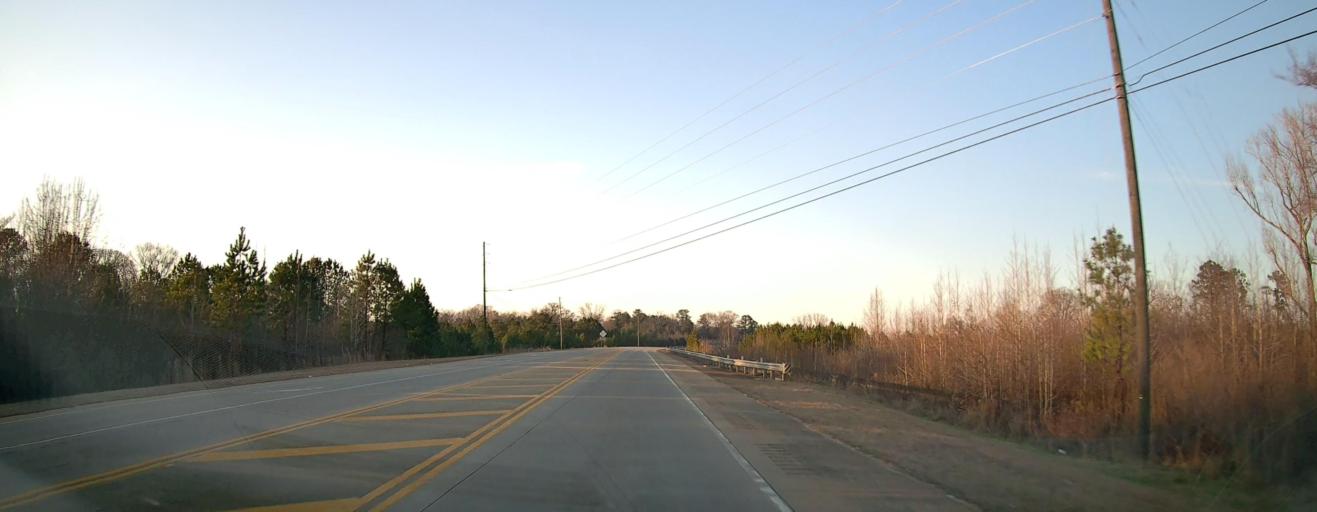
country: US
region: Georgia
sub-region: Troup County
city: La Grange
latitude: 33.0065
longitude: -85.0870
